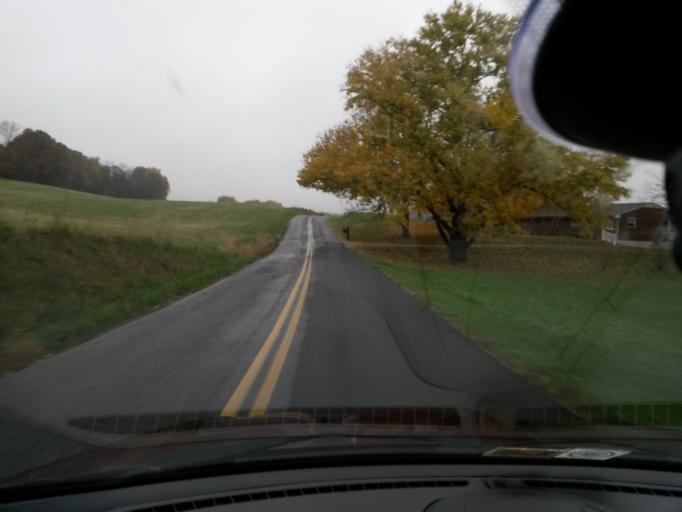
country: US
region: Virginia
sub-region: Botetourt County
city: Fincastle
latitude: 37.4750
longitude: -79.8516
